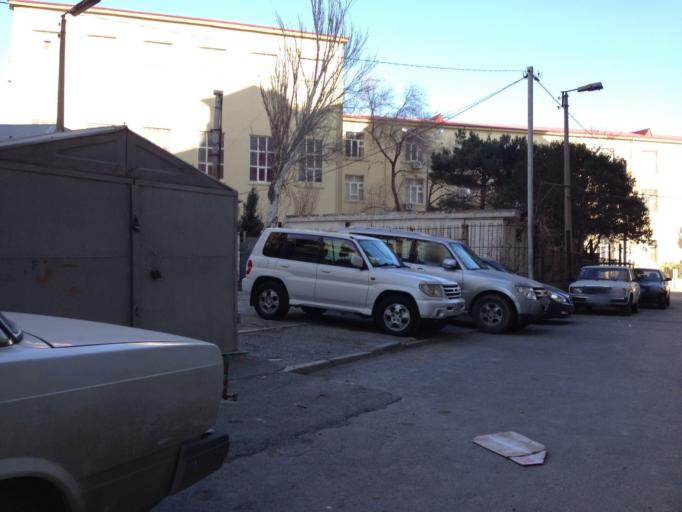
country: AZ
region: Baki
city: Baku
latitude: 40.3904
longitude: 49.8788
